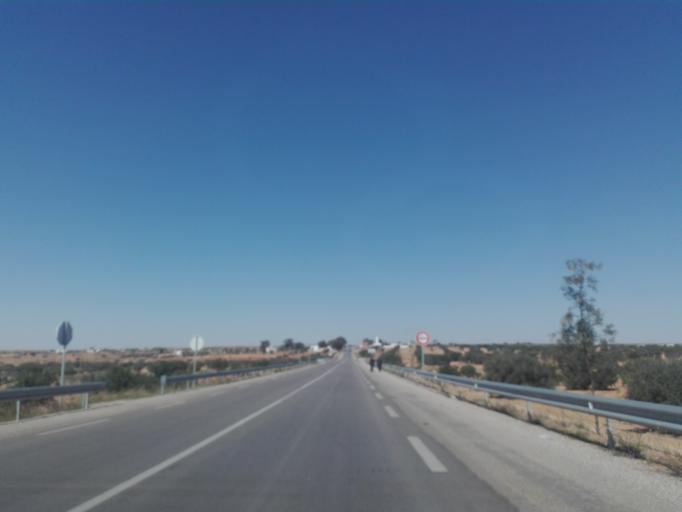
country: TN
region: Safaqis
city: Bi'r `Ali Bin Khalifah
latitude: 34.7411
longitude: 10.3796
